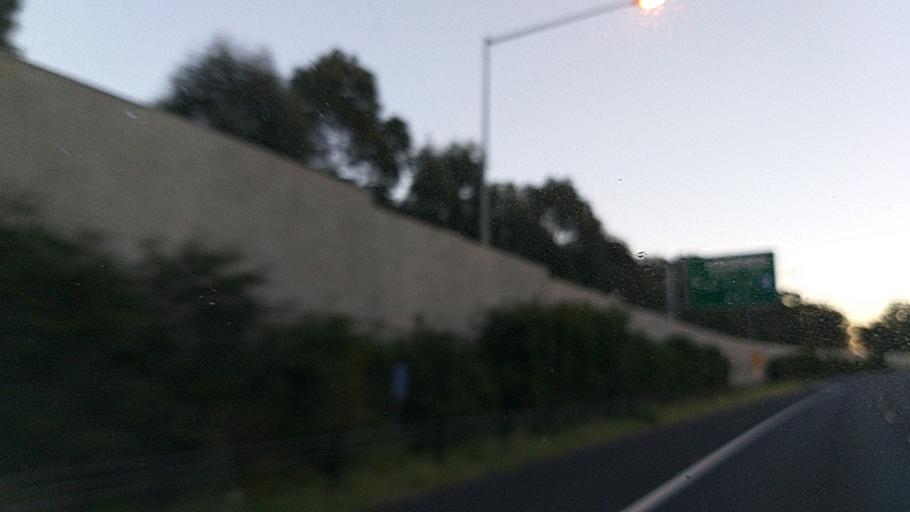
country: AU
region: New South Wales
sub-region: Blacktown
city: Glendenning
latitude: -33.7668
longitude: 150.8460
